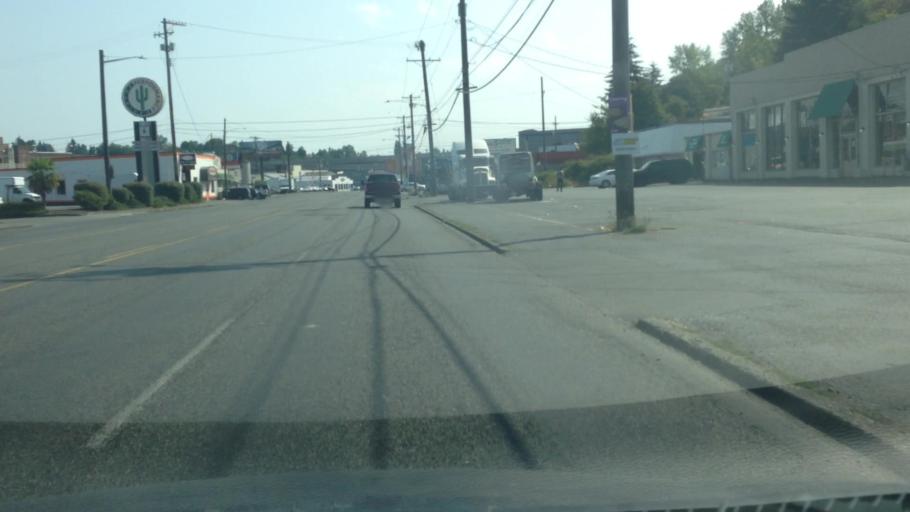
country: US
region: Washington
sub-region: Pierce County
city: Tacoma
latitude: 47.2300
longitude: -122.4728
